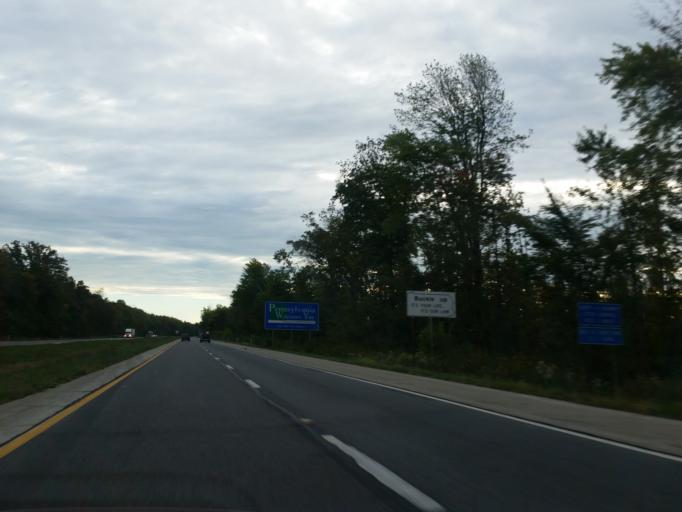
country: US
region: Ohio
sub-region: Ashtabula County
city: Conneaut
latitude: 41.9375
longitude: -80.5186
